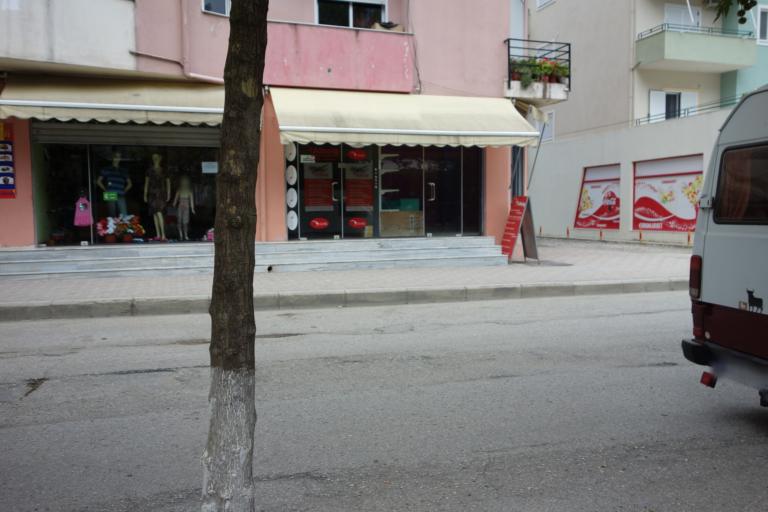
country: AL
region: Gjirokaster
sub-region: Rrethi i Permetit
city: Permet
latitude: 40.2318
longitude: 20.3556
